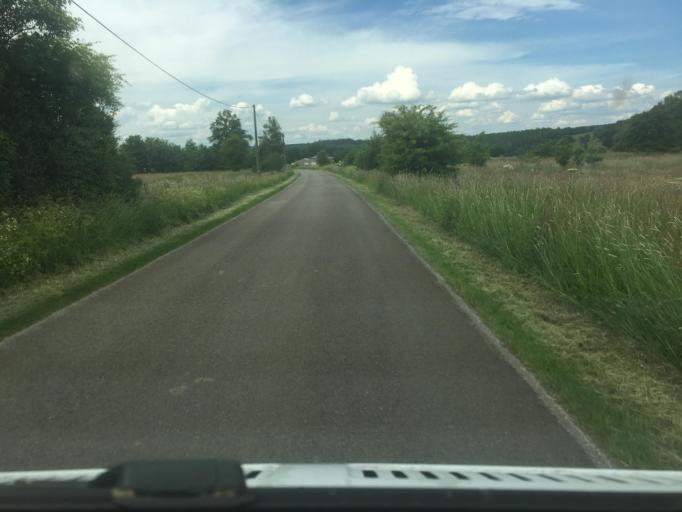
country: BE
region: Wallonia
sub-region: Province du Luxembourg
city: Florenville
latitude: 49.7156
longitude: 5.2597
